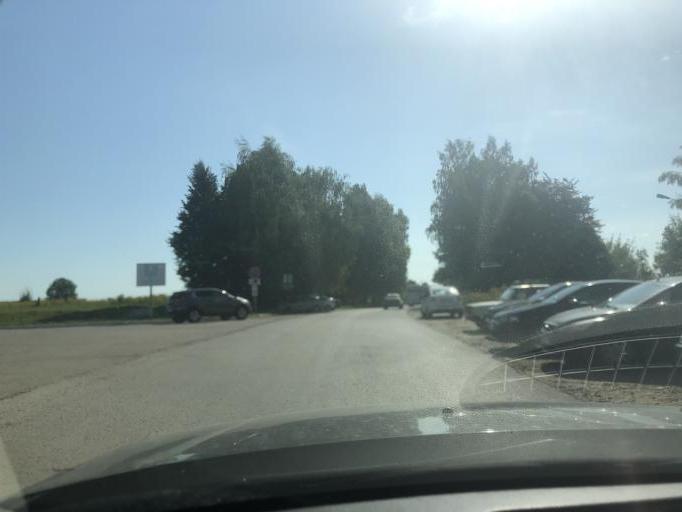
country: RU
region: Tula
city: Skuratovskiy
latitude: 54.1284
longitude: 37.6234
